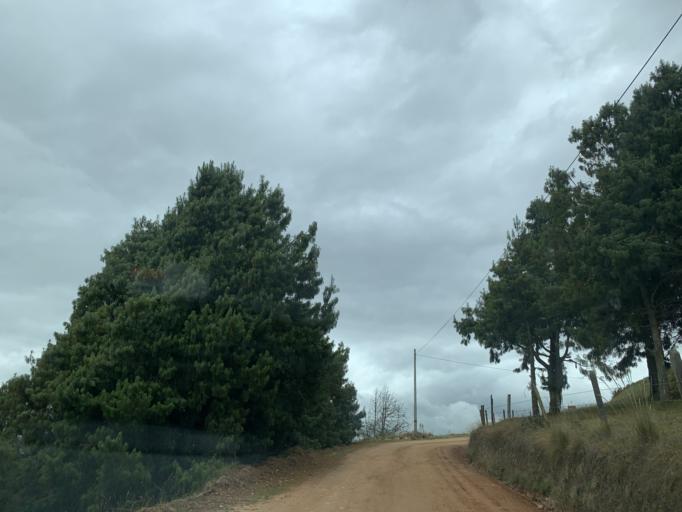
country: CO
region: Boyaca
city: Tunja
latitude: 5.5295
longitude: -73.3200
